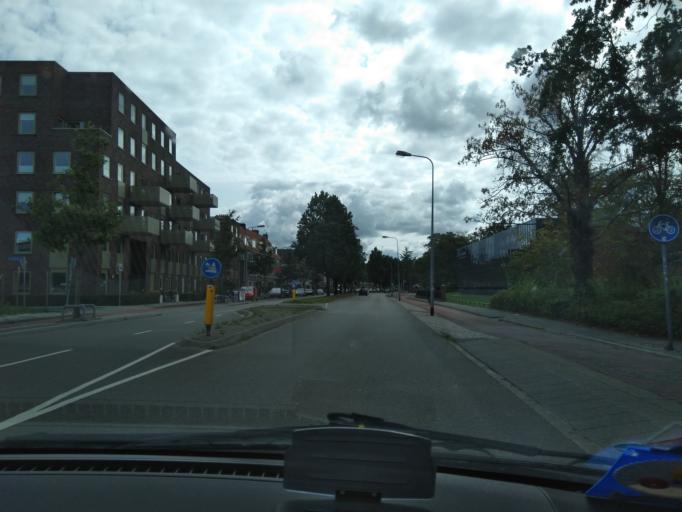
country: NL
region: Groningen
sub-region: Gemeente Groningen
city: Groningen
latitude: 53.2082
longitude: 6.5576
